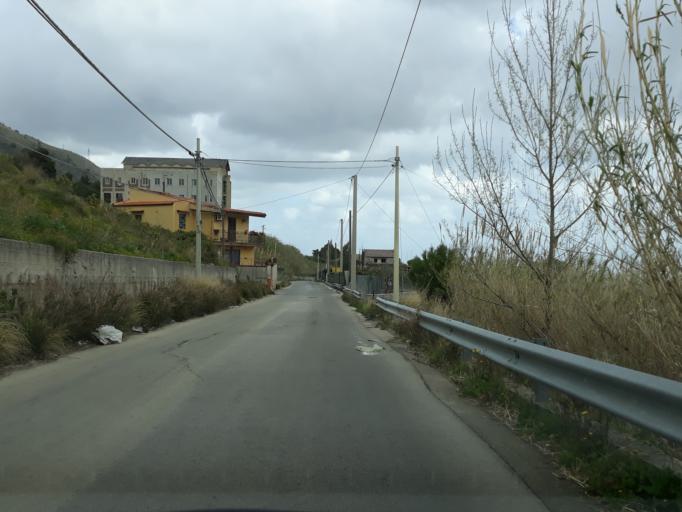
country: IT
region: Sicily
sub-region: Palermo
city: Monreale
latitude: 38.0781
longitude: 13.2921
